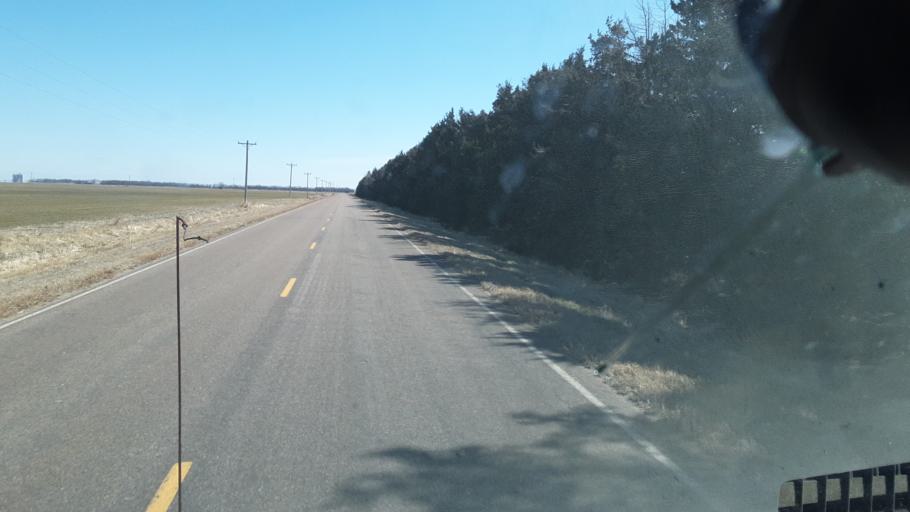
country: US
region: Kansas
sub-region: Rice County
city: Sterling
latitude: 38.2461
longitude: -98.2602
